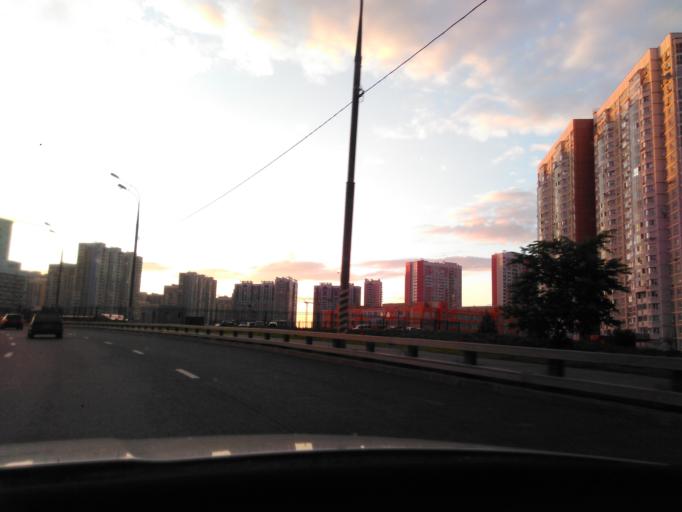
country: RU
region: Moscow
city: Khimki
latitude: 55.9005
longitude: 37.3983
